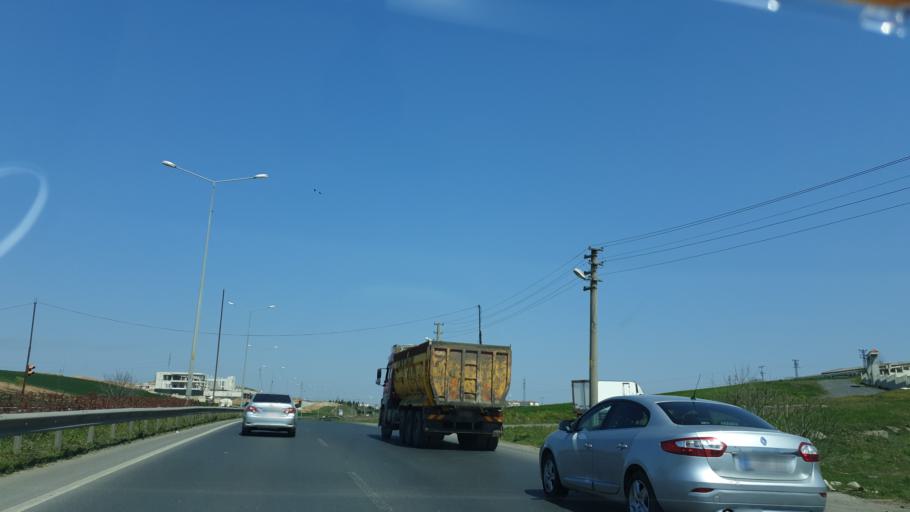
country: TR
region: Tekirdag
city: Corlu
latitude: 41.1718
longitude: 27.8013
